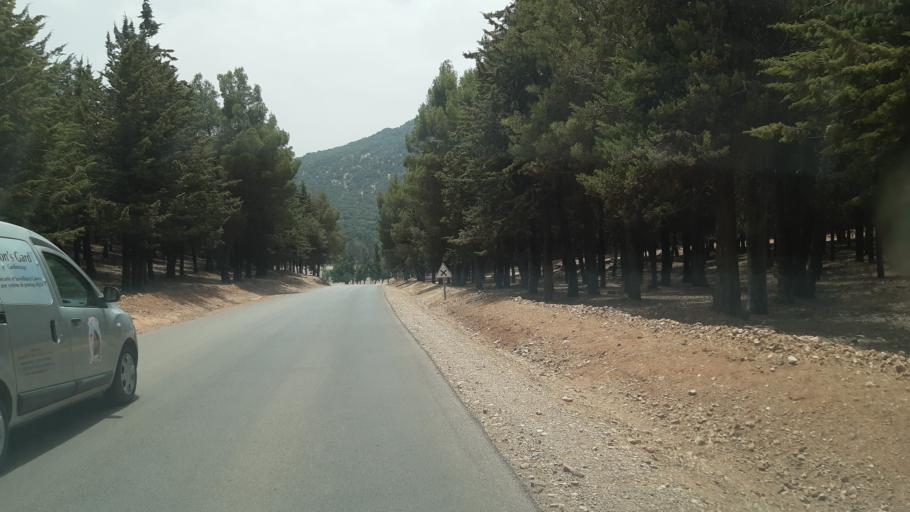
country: MA
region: Meknes-Tafilalet
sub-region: Ifrane
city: Ifrane
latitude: 33.6597
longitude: -5.0430
